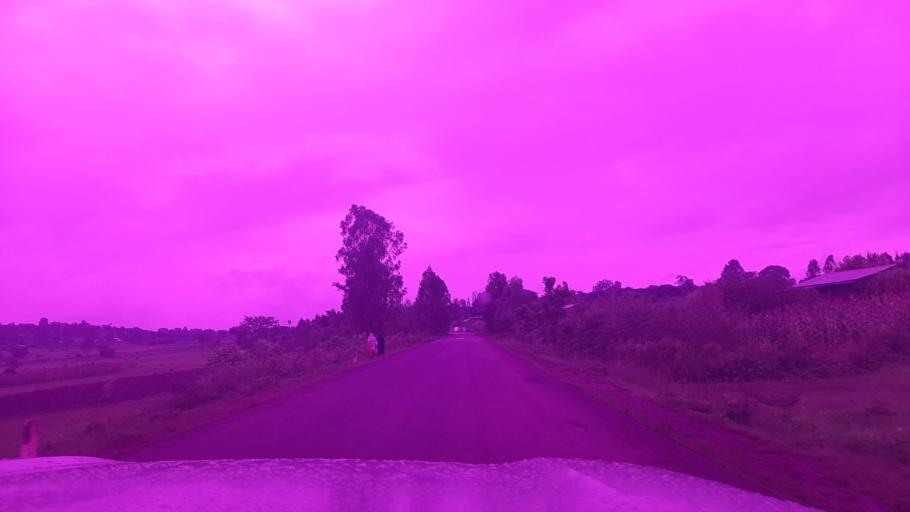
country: ET
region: Oromiya
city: Jima
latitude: 7.7315
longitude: 37.2702
